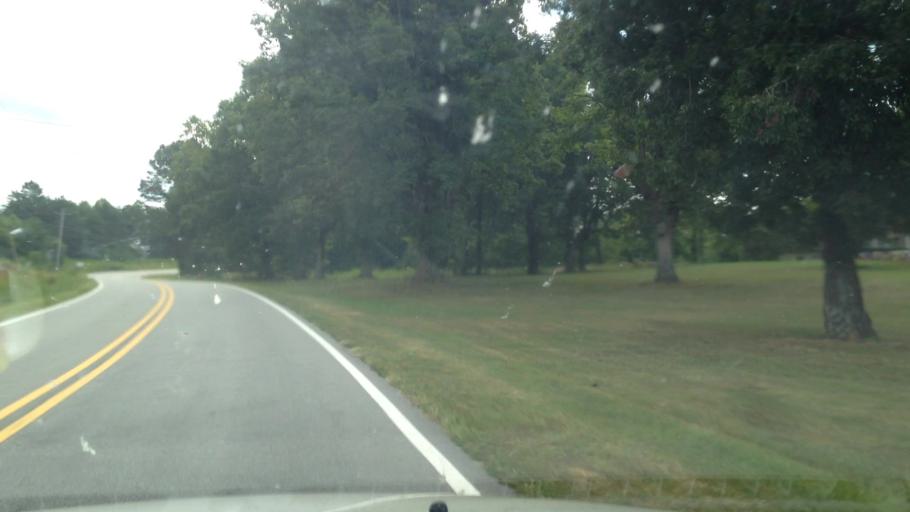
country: US
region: North Carolina
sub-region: Rockingham County
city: Mayodan
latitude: 36.3965
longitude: -80.0279
